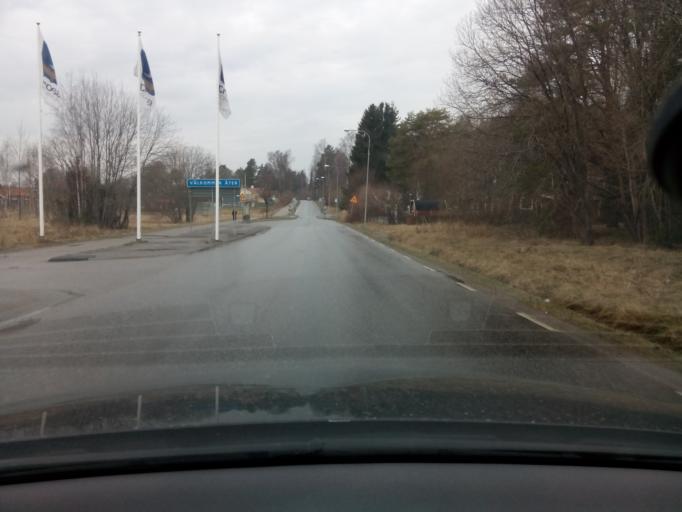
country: SE
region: Soedermanland
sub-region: Trosa Kommun
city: Trosa
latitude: 58.9002
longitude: 17.5298
